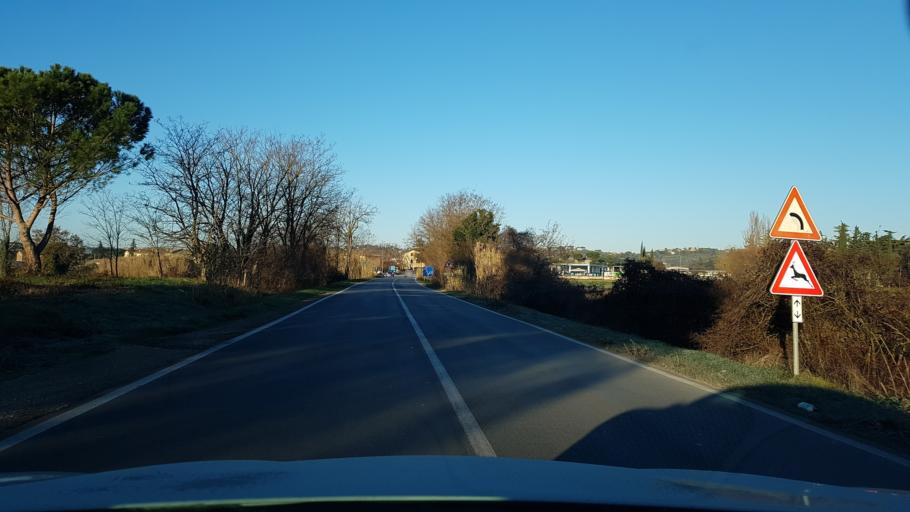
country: IT
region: Umbria
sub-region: Provincia di Perugia
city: San Martino in Campo
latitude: 43.0361
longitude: 12.4184
